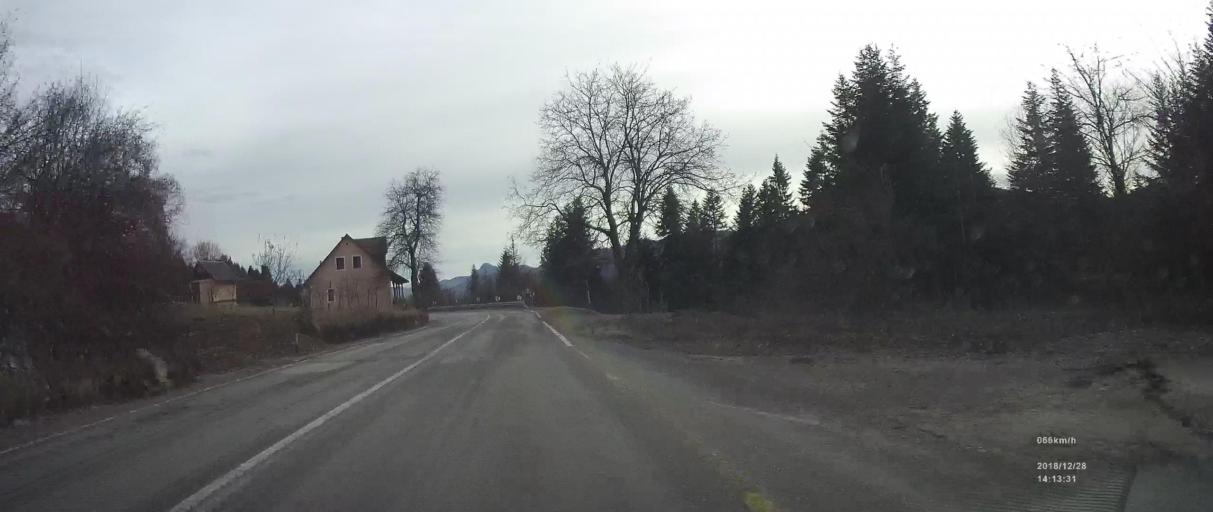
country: HR
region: Primorsko-Goranska
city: Vrbovsko
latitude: 45.4388
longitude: 15.0079
